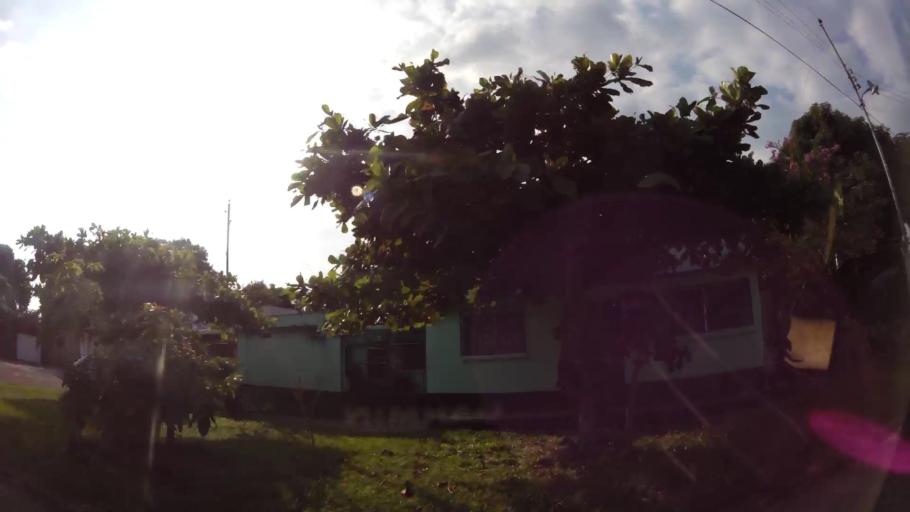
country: GT
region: Retalhuleu
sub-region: Municipio de Retalhuleu
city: Retalhuleu
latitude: 14.5439
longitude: -91.6762
